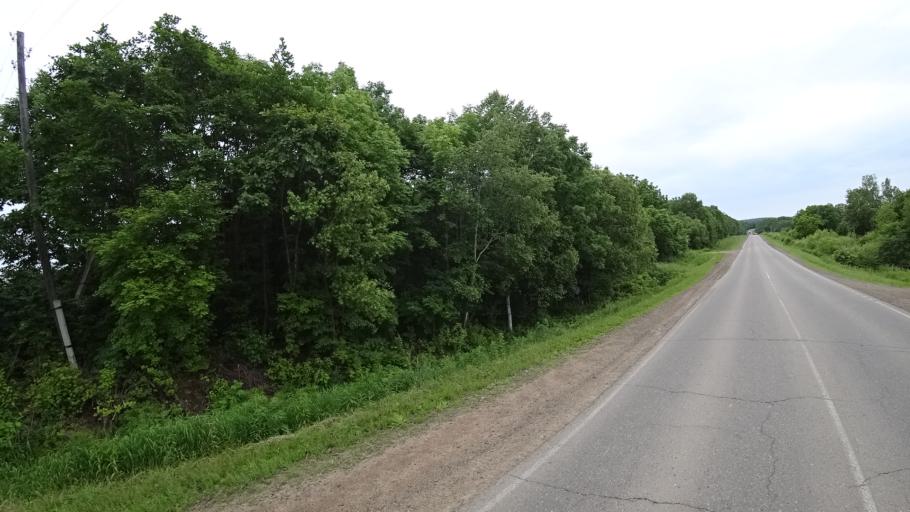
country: RU
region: Primorskiy
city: Novosysoyevka
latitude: 44.1786
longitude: 133.3478
